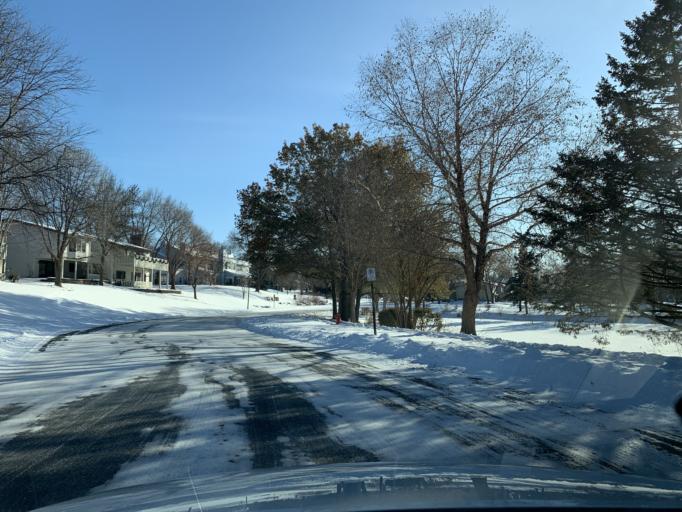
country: US
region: Minnesota
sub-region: Scott County
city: Savage
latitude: 44.8291
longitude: -93.3532
